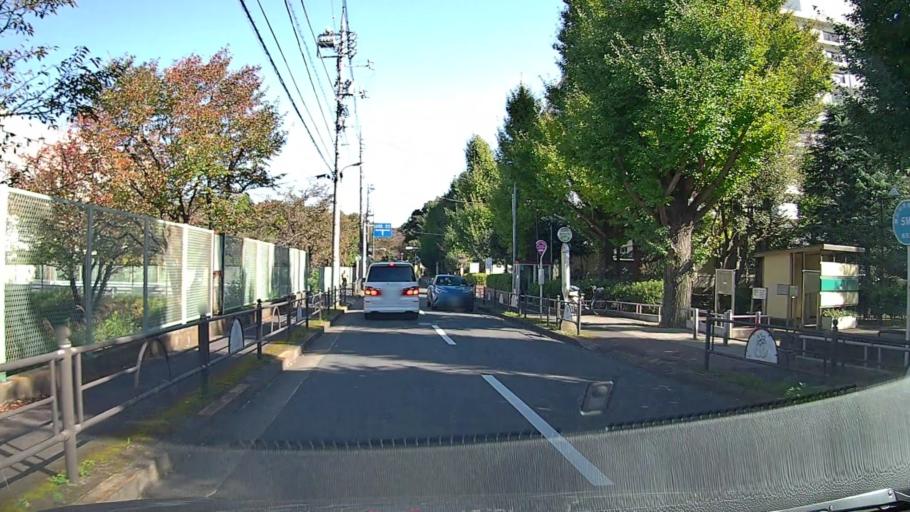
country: JP
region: Saitama
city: Wako
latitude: 35.7667
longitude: 139.6238
